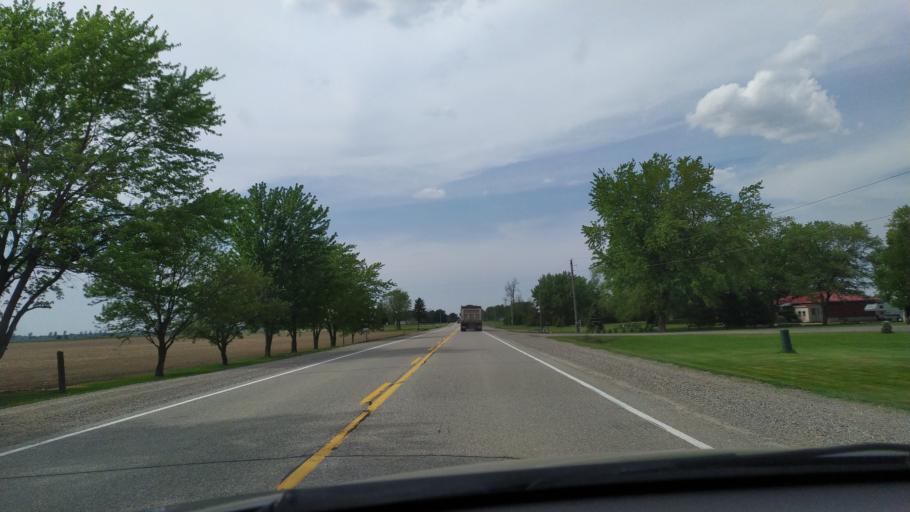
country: CA
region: Ontario
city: Stratford
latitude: 43.2280
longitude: -81.0749
